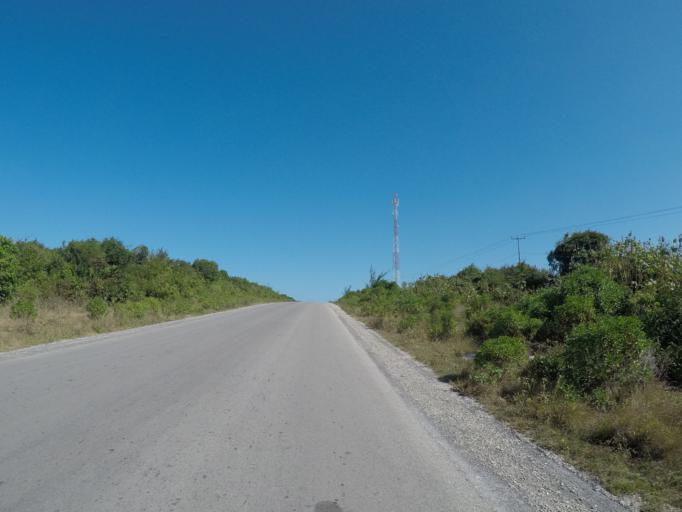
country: TZ
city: Kiwengwa
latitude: -6.1573
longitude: 39.5191
